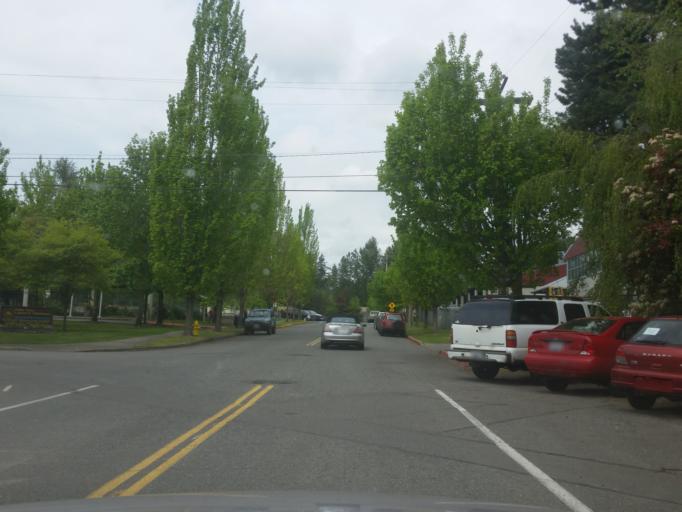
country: US
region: Washington
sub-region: King County
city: Kirkland
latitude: 47.6821
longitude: -122.1932
